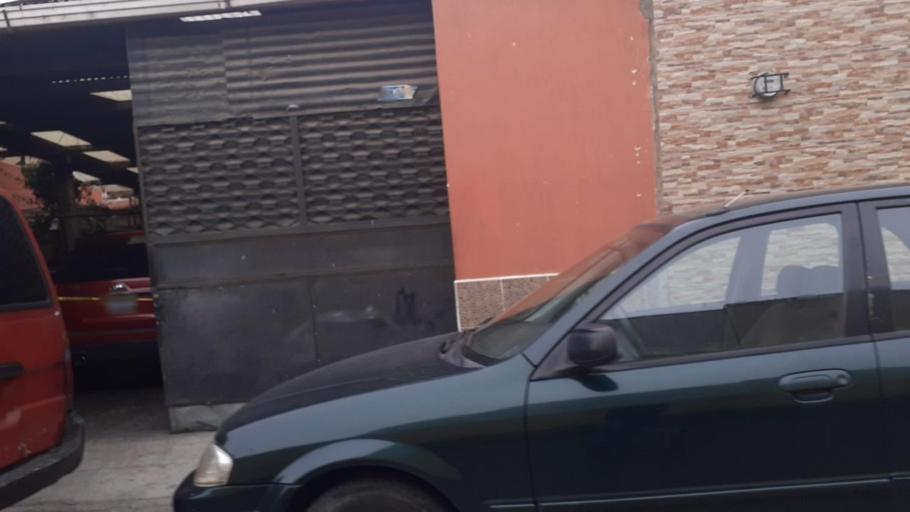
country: GT
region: Quetzaltenango
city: Quetzaltenango
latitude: 14.8388
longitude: -91.5254
